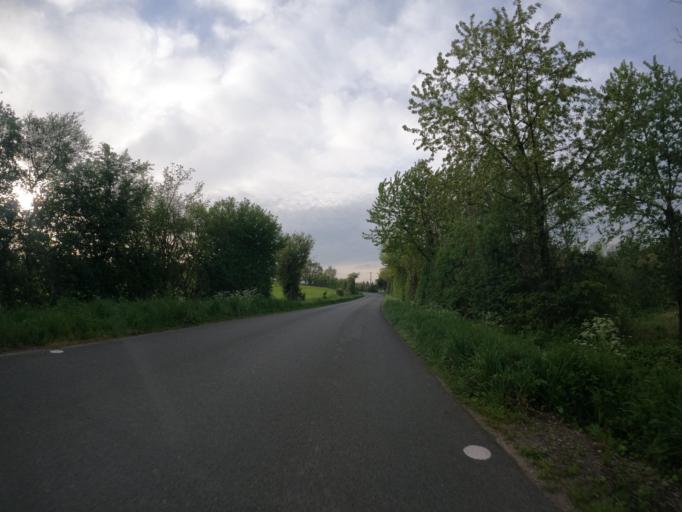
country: FR
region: Poitou-Charentes
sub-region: Departement des Deux-Sevres
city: Moncoutant
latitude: 46.6996
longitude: -0.5255
